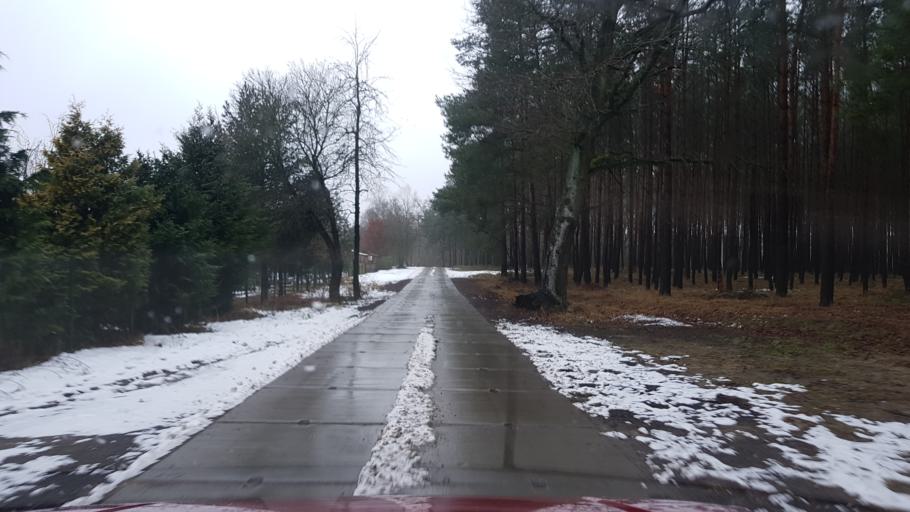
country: PL
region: West Pomeranian Voivodeship
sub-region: Powiat policki
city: Dobra
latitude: 53.5542
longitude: 14.4034
